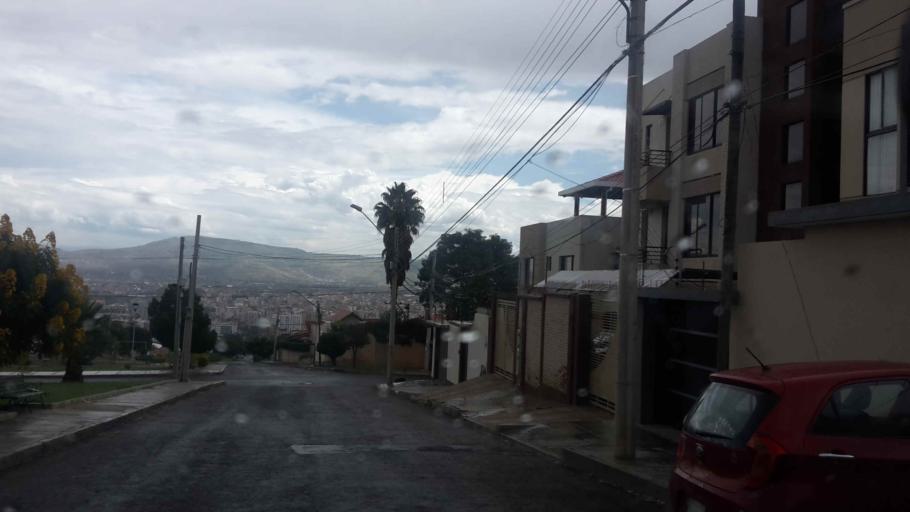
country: BO
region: Cochabamba
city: Cochabamba
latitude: -17.3578
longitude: -66.1582
